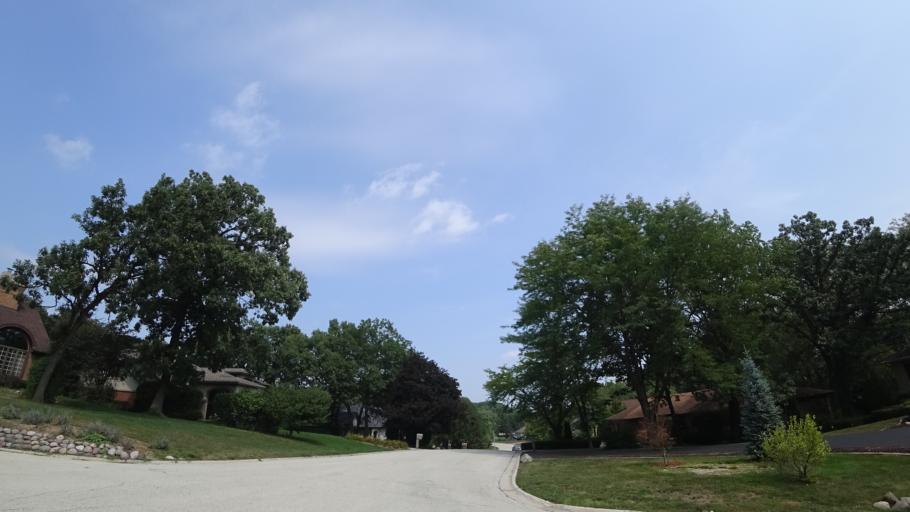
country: US
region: Illinois
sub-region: Cook County
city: Orland Park
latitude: 41.6186
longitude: -87.8718
